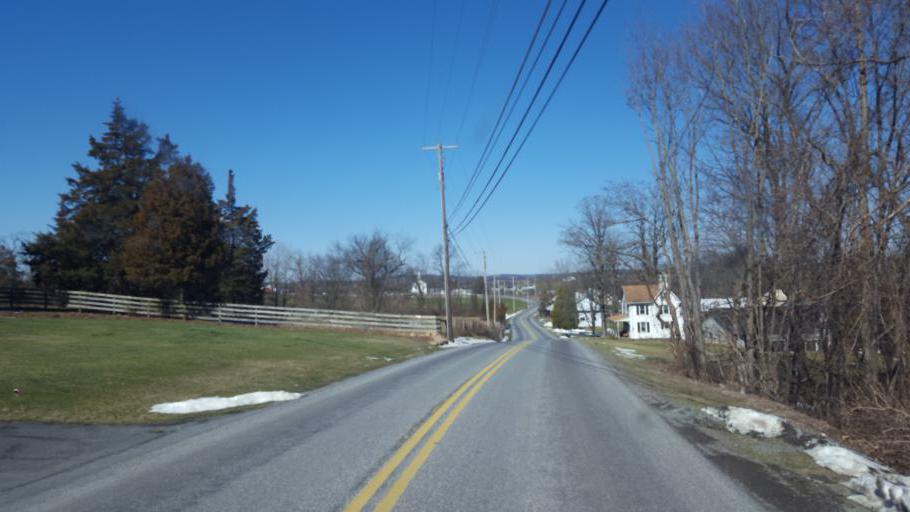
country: US
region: Pennsylvania
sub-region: Lancaster County
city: Bowmansville
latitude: 40.1603
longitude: -76.0075
